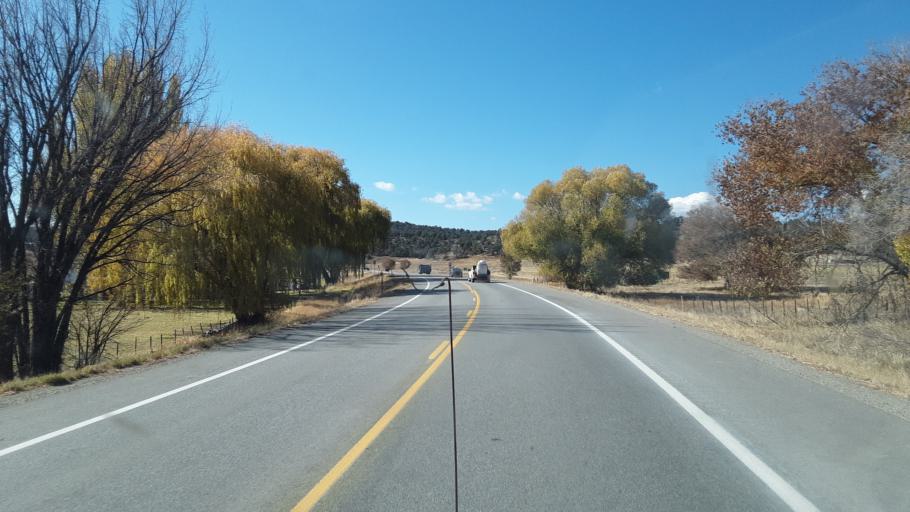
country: US
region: Colorado
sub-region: La Plata County
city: Bayfield
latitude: 37.2258
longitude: -107.6606
